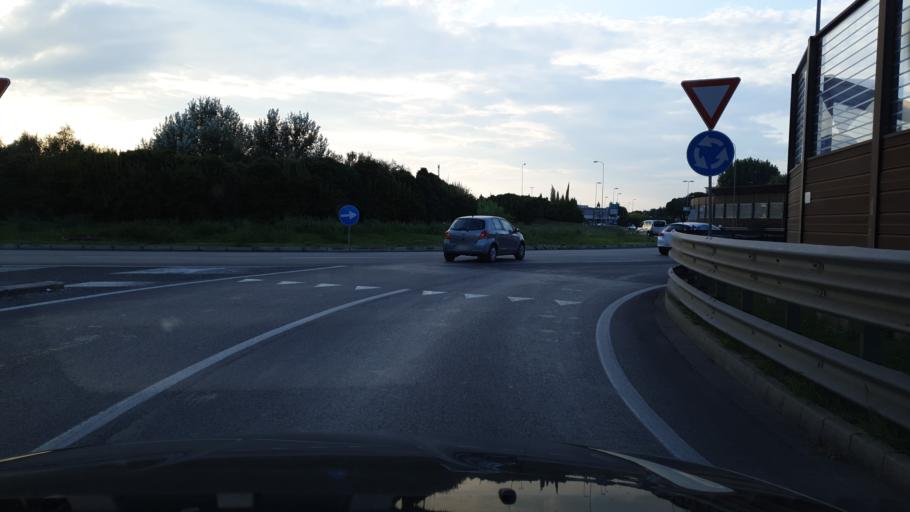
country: IT
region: Emilia-Romagna
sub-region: Provincia di Rimini
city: Rivazzurra
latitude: 44.0405
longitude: 12.5918
